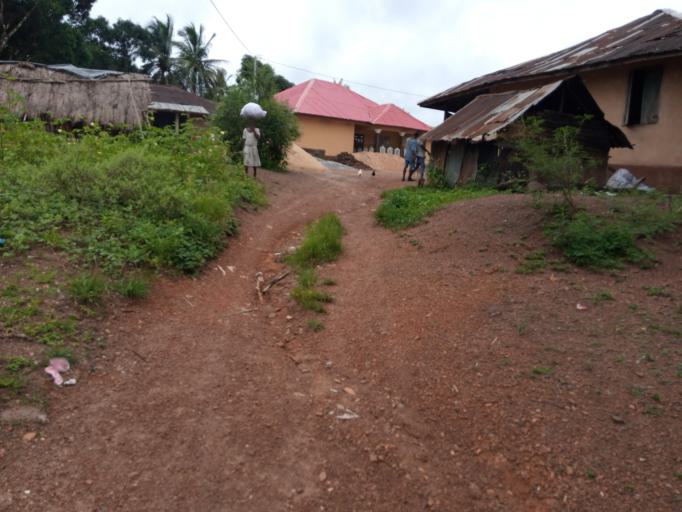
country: SL
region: Southern Province
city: Largo
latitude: 8.2050
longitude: -12.0585
